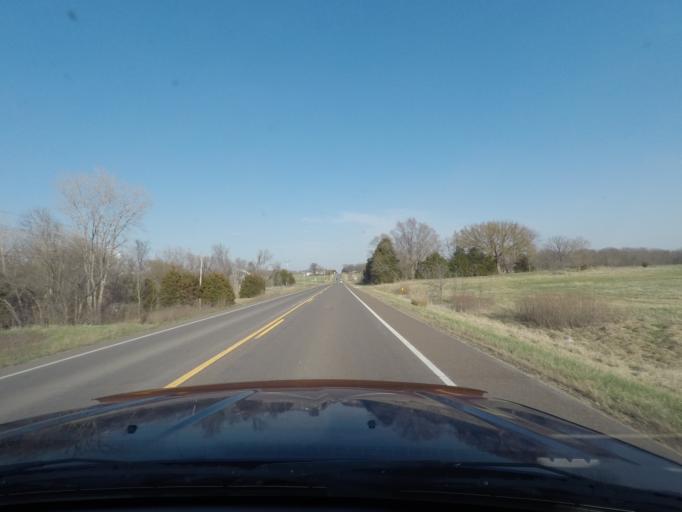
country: US
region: Kansas
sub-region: Douglas County
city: Lawrence
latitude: 39.0006
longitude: -95.2857
